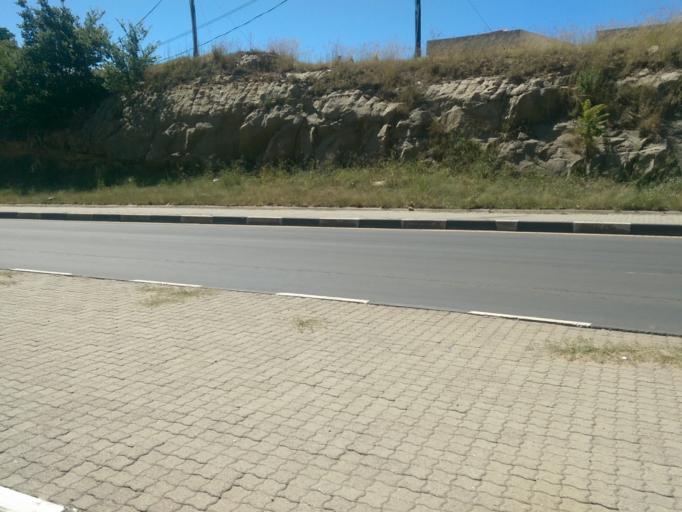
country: LS
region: Maseru
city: Maseru
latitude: -29.3170
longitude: 27.4852
